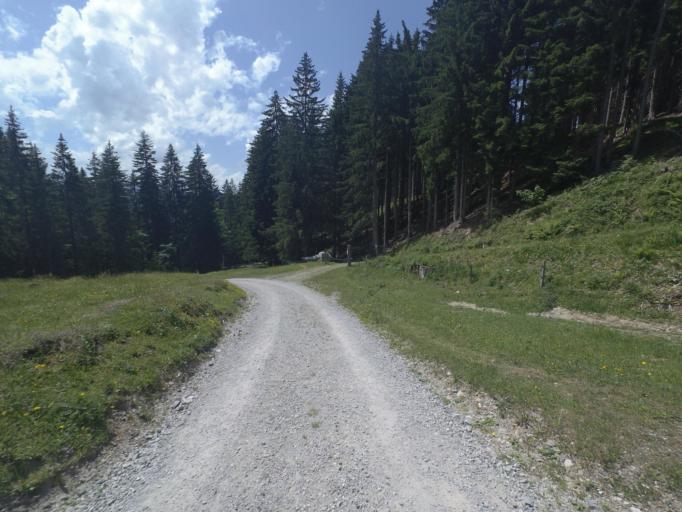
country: AT
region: Salzburg
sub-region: Politischer Bezirk Zell am See
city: Dienten am Hochkonig
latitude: 47.4120
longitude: 12.9926
